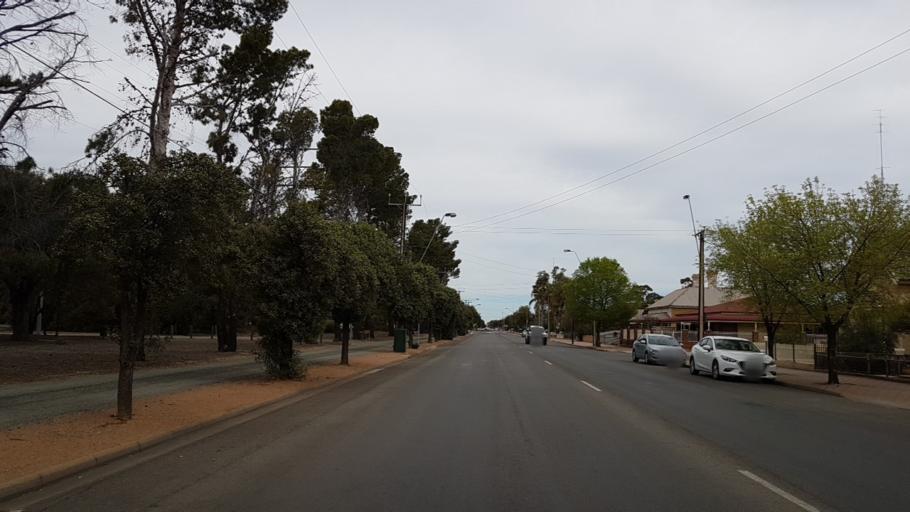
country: AU
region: South Australia
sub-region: Port Pirie City and Dists
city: Port Pirie
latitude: -33.1791
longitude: 138.0039
